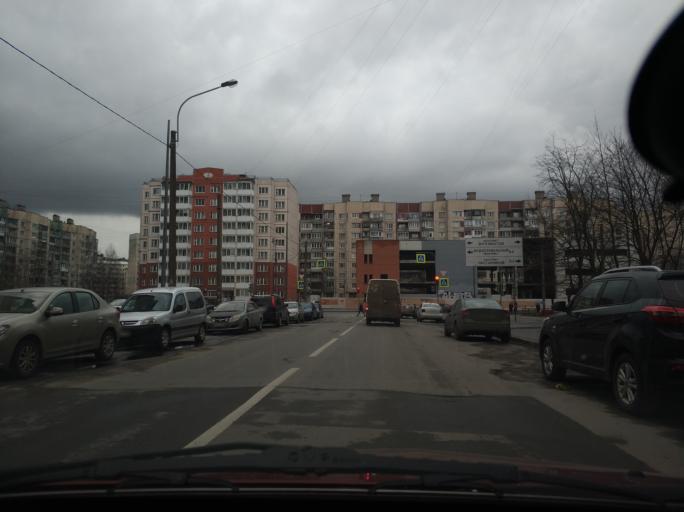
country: RU
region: St.-Petersburg
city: Krasnogvargeisky
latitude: 59.9486
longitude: 30.4819
